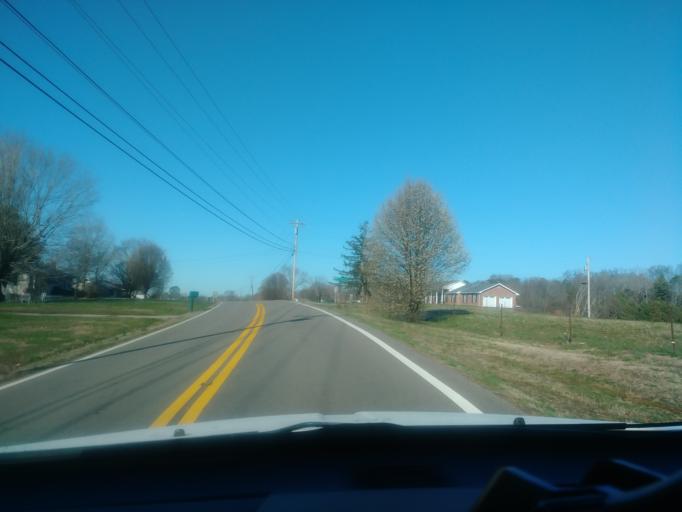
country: US
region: Tennessee
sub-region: Greene County
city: Mosheim
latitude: 36.1157
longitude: -82.9578
